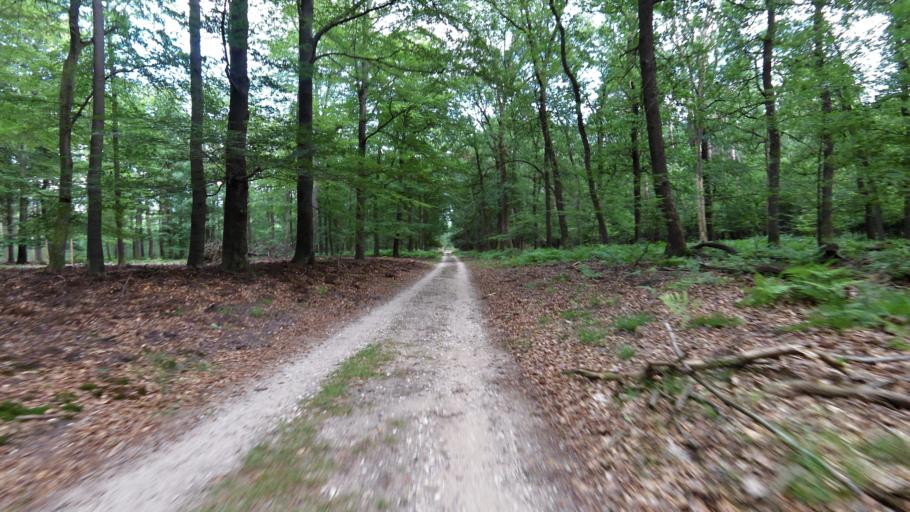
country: NL
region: Gelderland
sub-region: Gemeente Apeldoorn
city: Uddel
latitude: 52.2385
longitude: 5.8716
